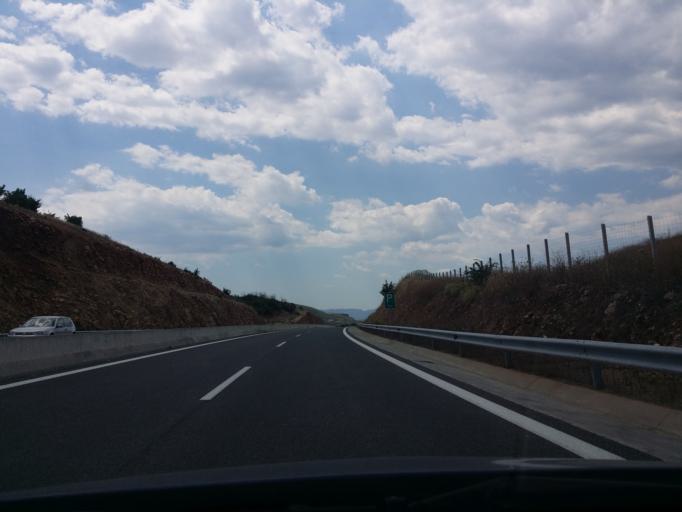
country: GR
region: Peloponnese
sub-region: Nomos Arkadias
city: Megalopoli
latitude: 37.3070
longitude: 22.1842
